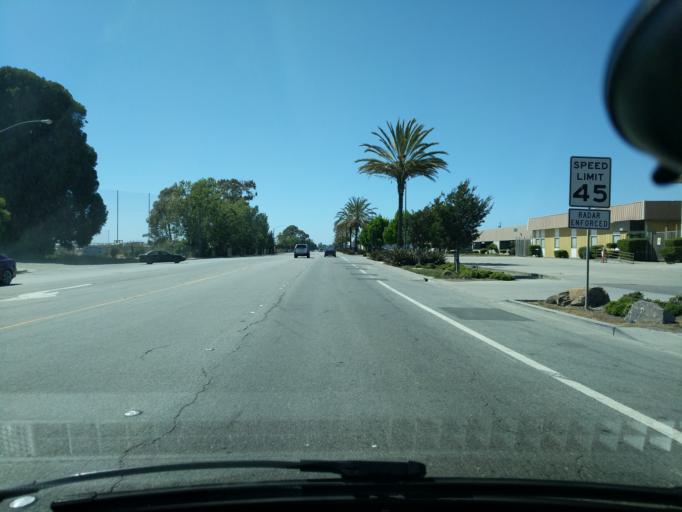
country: US
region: California
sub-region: Alameda County
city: San Leandro
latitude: 37.7176
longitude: -122.1886
